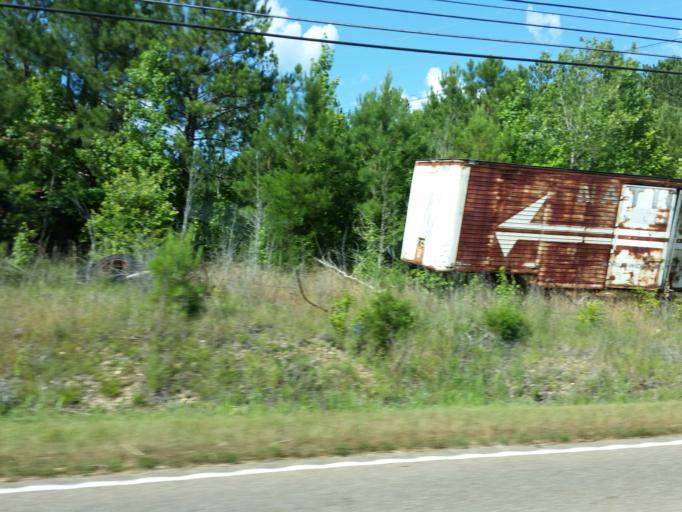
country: US
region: Tennessee
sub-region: Decatur County
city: Parsons
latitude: 35.6446
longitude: -88.0999
